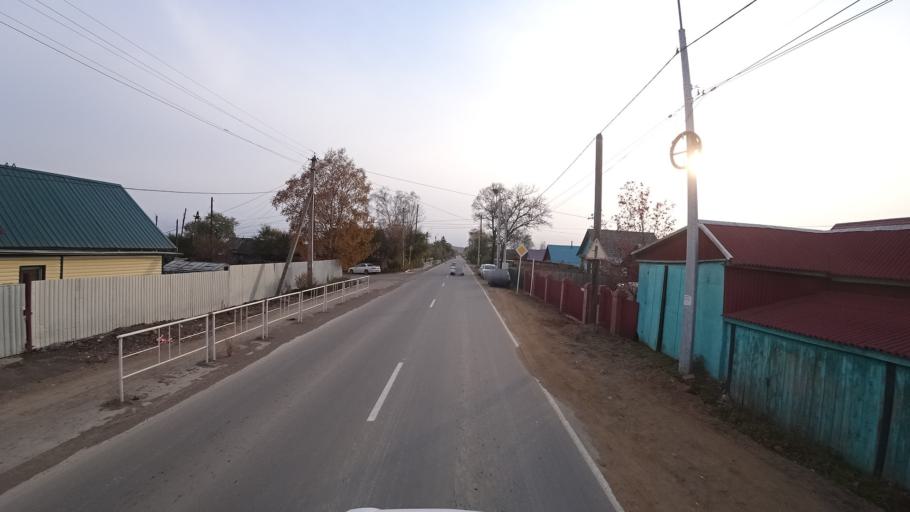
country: RU
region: Khabarovsk Krai
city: Amursk
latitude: 50.0910
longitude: 136.5028
